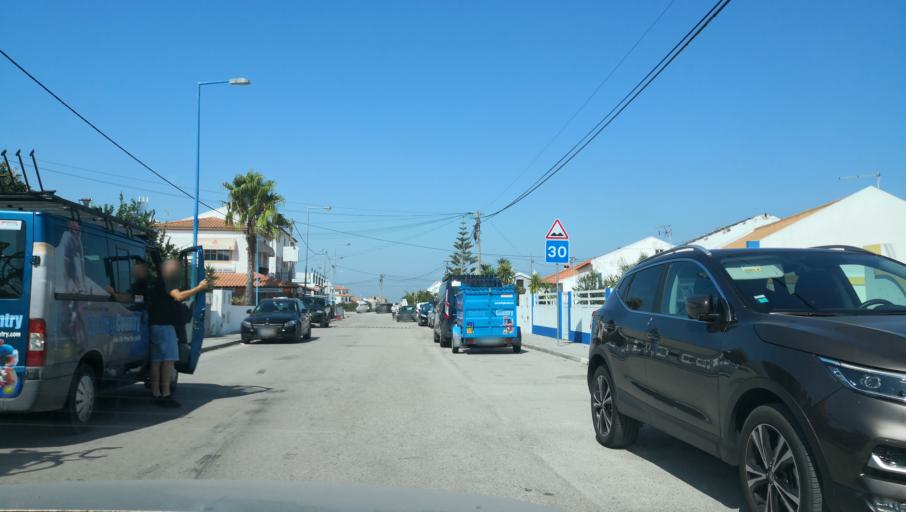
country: PT
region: Setubal
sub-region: Setubal
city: Setubal
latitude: 38.4078
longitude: -8.7478
